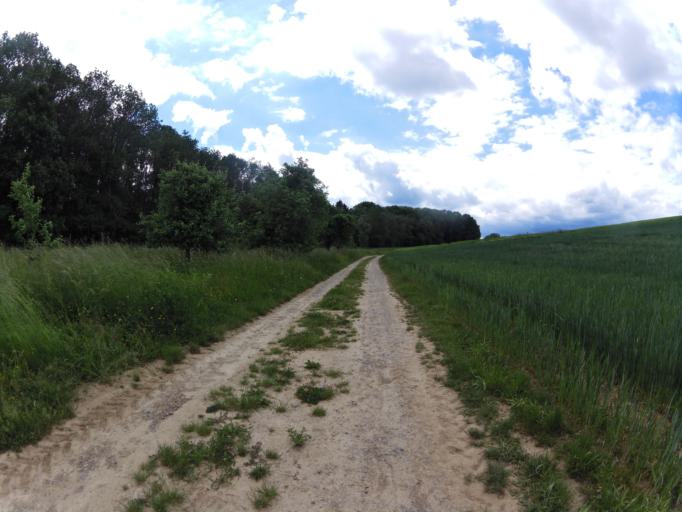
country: DE
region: Bavaria
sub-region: Regierungsbezirk Unterfranken
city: Gaukonigshofen
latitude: 49.6701
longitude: 9.9981
